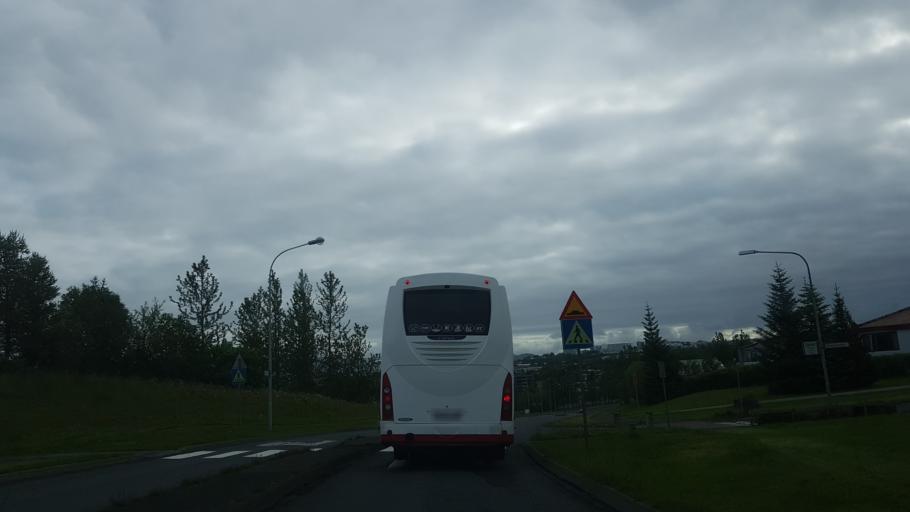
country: IS
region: Capital Region
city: Reykjavik
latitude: 64.1015
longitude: -21.8565
